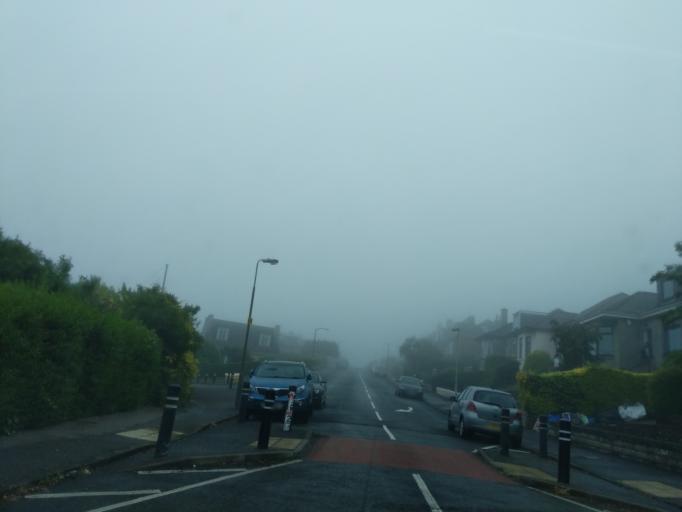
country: GB
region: Scotland
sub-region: West Lothian
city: Seafield
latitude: 55.9508
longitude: -3.1482
